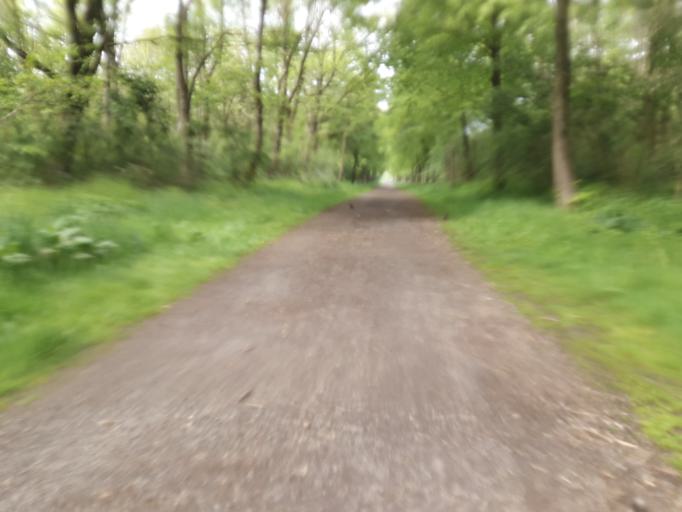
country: DE
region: North Rhine-Westphalia
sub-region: Regierungsbezirk Detmold
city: Paderborn
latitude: 51.6937
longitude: 8.7601
